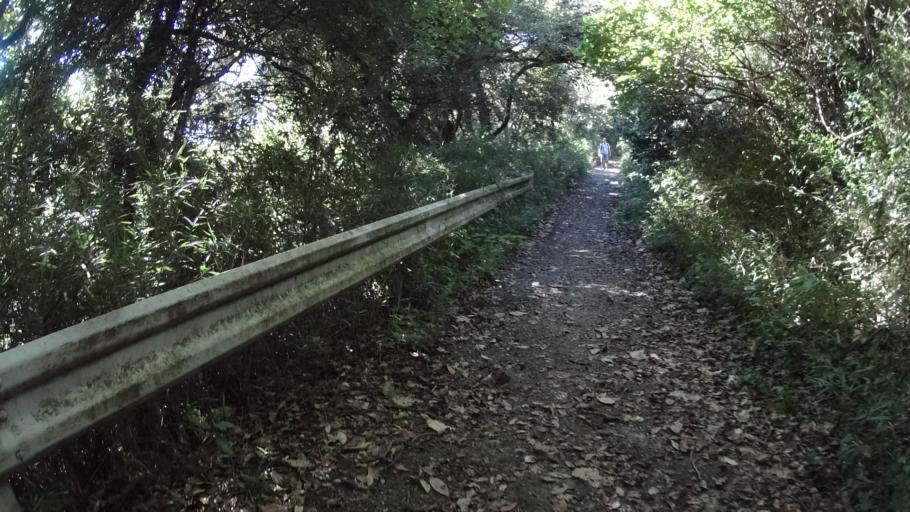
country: JP
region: Kanagawa
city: Zushi
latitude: 35.2865
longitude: 139.6056
